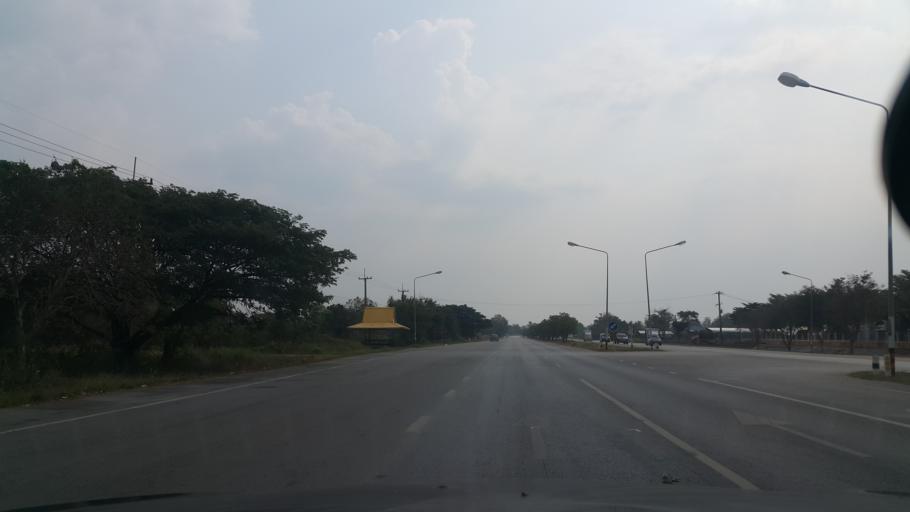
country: TH
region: Sukhothai
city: Sukhothai
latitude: 17.0608
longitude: 99.8901
